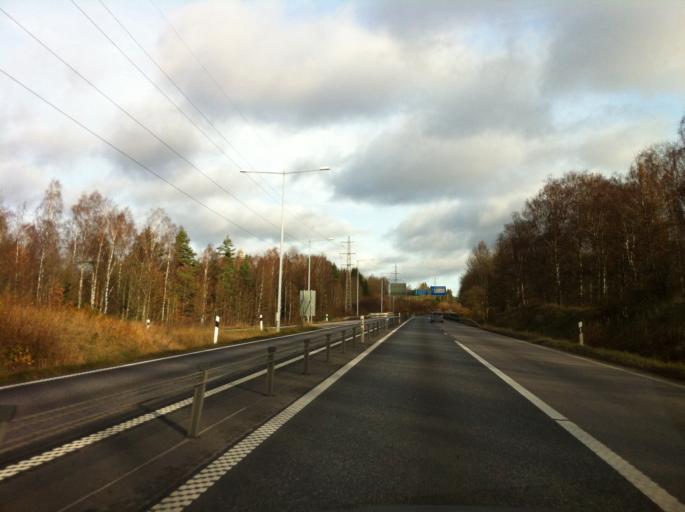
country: SE
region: Kronoberg
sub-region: Vaxjo Kommun
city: Gemla
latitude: 56.8271
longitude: 14.6922
